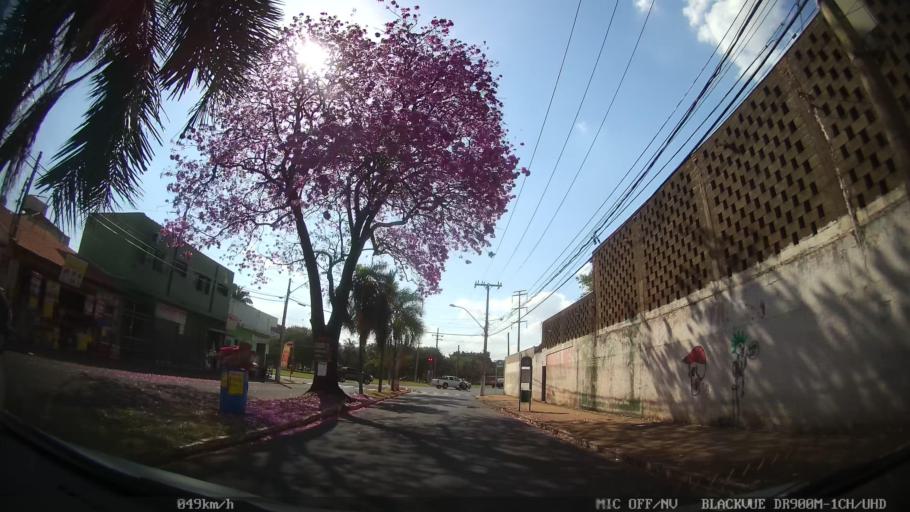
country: BR
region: Sao Paulo
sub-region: Ribeirao Preto
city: Ribeirao Preto
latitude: -21.1790
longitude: -47.8224
